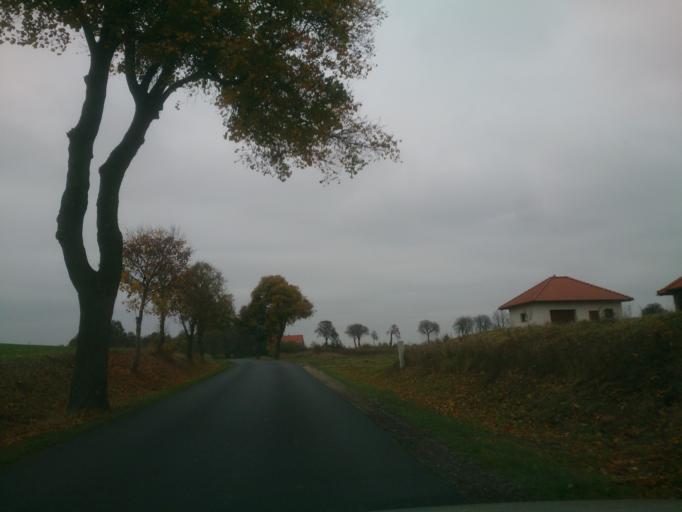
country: PL
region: Kujawsko-Pomorskie
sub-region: Powiat brodnicki
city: Brodnica
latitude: 53.2950
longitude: 19.3964
